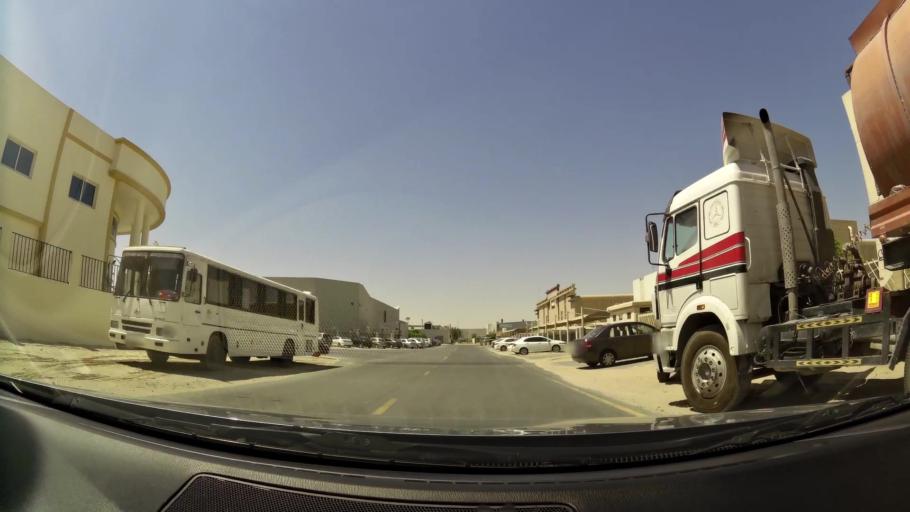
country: AE
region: Dubai
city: Dubai
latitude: 24.9875
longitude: 55.1938
